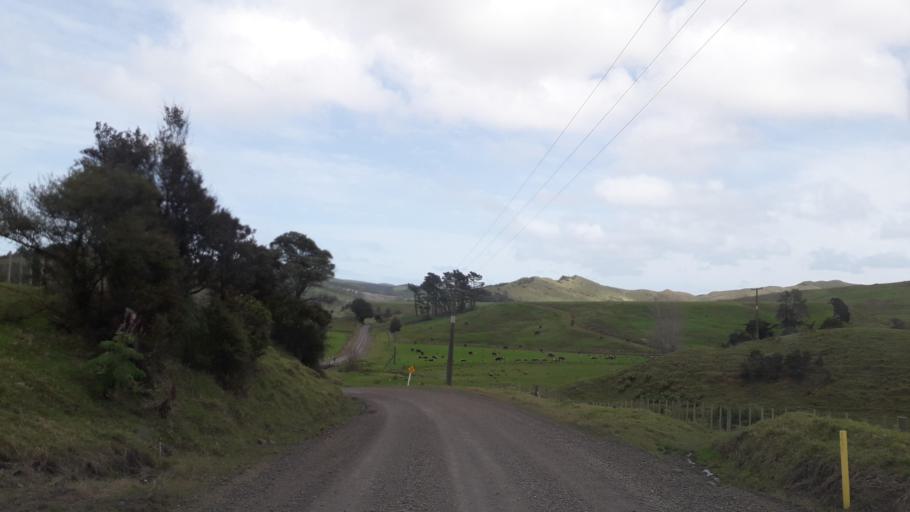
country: NZ
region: Northland
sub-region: Far North District
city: Kaitaia
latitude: -35.4152
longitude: 173.3650
